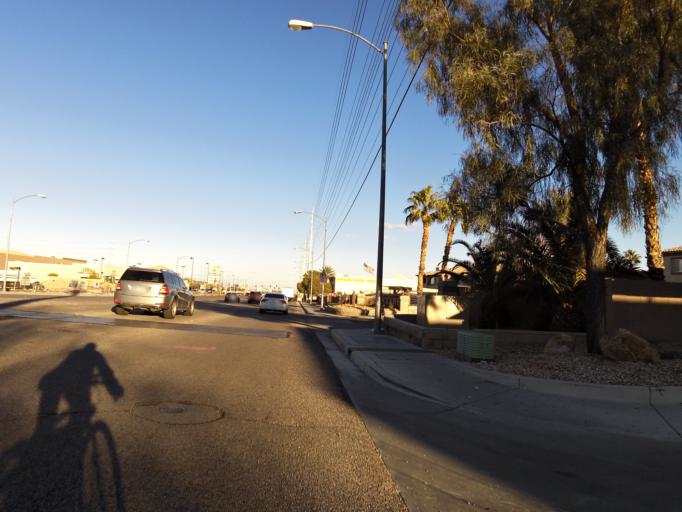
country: US
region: Nevada
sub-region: Clark County
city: Spring Valley
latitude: 36.1148
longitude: -115.2826
